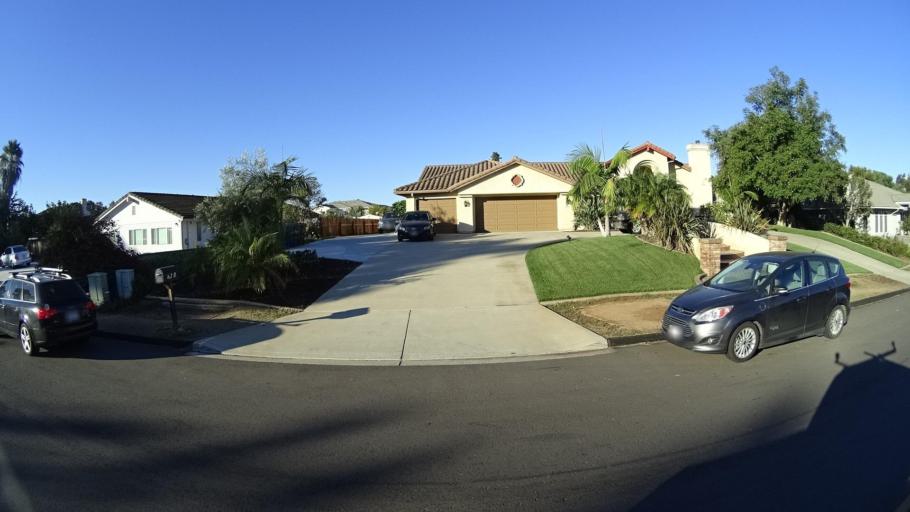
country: US
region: California
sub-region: San Diego County
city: Bonita
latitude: 32.6688
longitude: -117.0295
